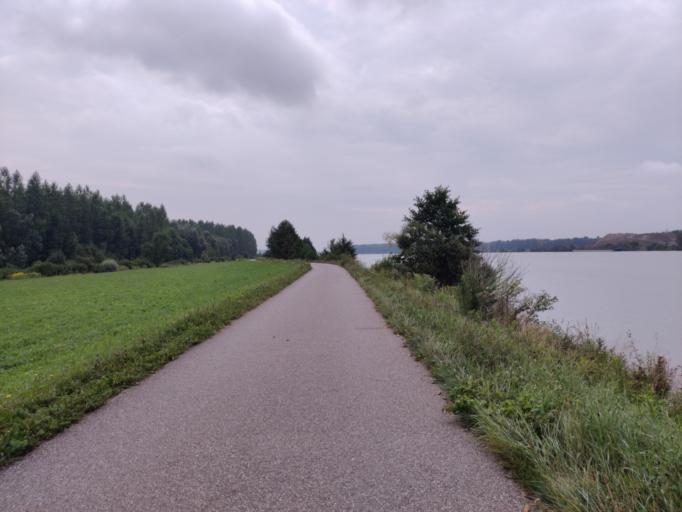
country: AT
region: Upper Austria
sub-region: Politischer Bezirk Urfahr-Umgebung
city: Steyregg
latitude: 48.2759
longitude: 14.3588
